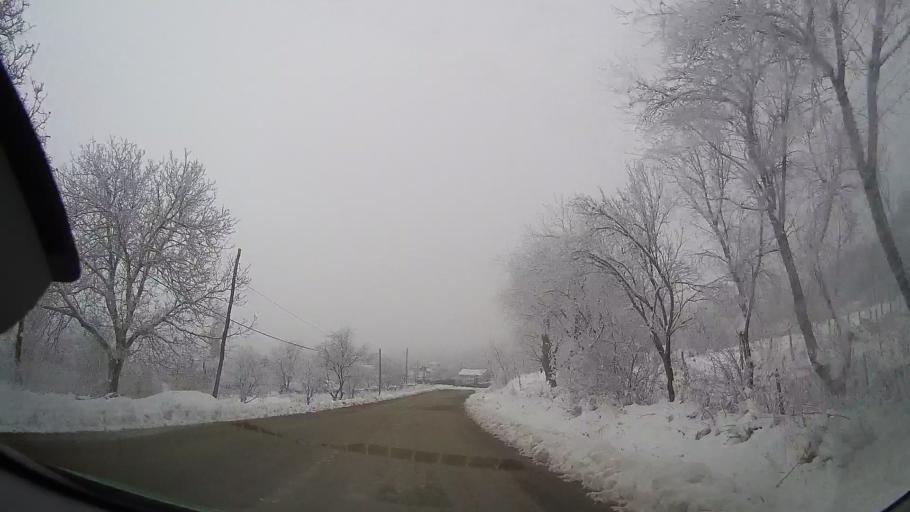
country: RO
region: Iasi
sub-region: Comuna Tansa
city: Suhulet
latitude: 46.9016
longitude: 27.2420
